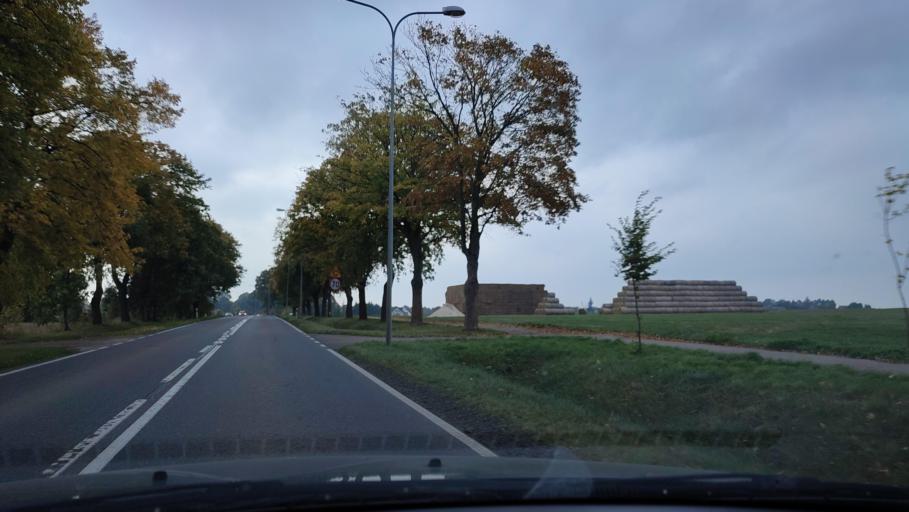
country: PL
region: Warmian-Masurian Voivodeship
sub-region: Powiat nidzicki
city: Nidzica
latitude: 53.3529
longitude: 20.3650
